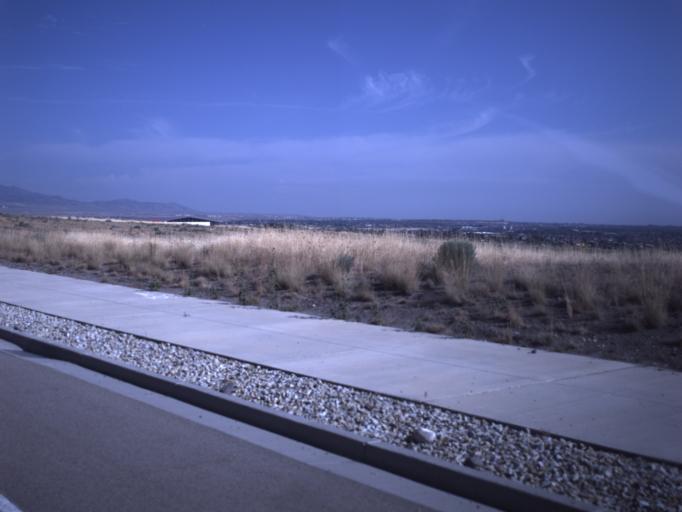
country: US
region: Utah
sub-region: Salt Lake County
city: Bluffdale
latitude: 40.4713
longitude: -111.9683
